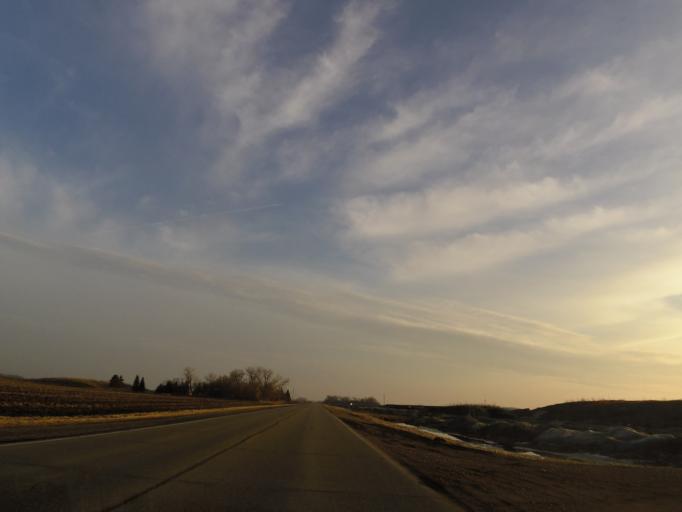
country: US
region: North Dakota
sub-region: Grand Forks County
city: Grand Forks
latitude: 47.8651
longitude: -97.0453
